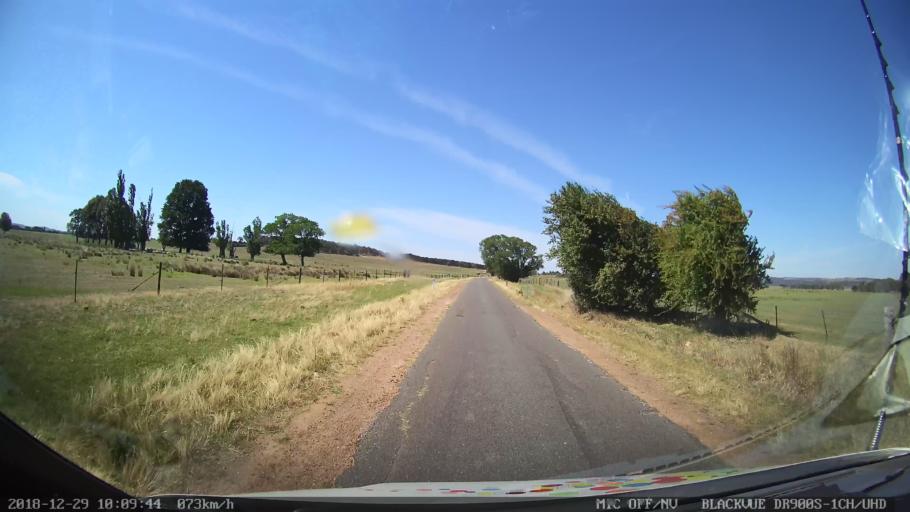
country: AU
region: New South Wales
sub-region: Yass Valley
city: Gundaroo
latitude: -34.8688
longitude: 149.4593
